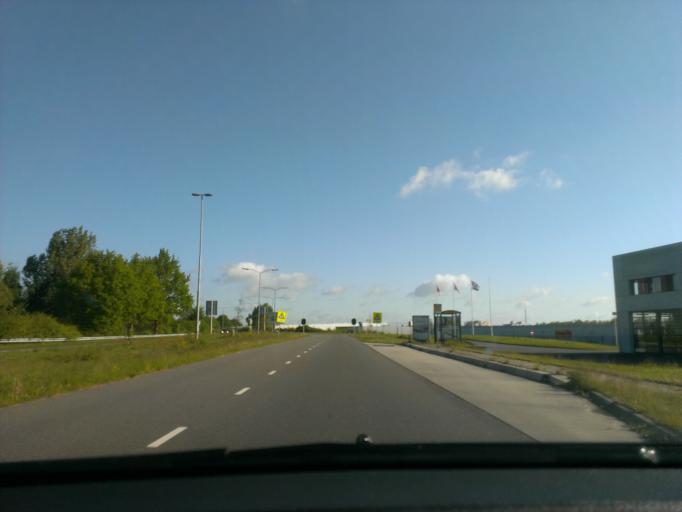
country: NL
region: Drenthe
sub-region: Gemeente Emmen
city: Emmen
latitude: 52.7616
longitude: 6.8982
